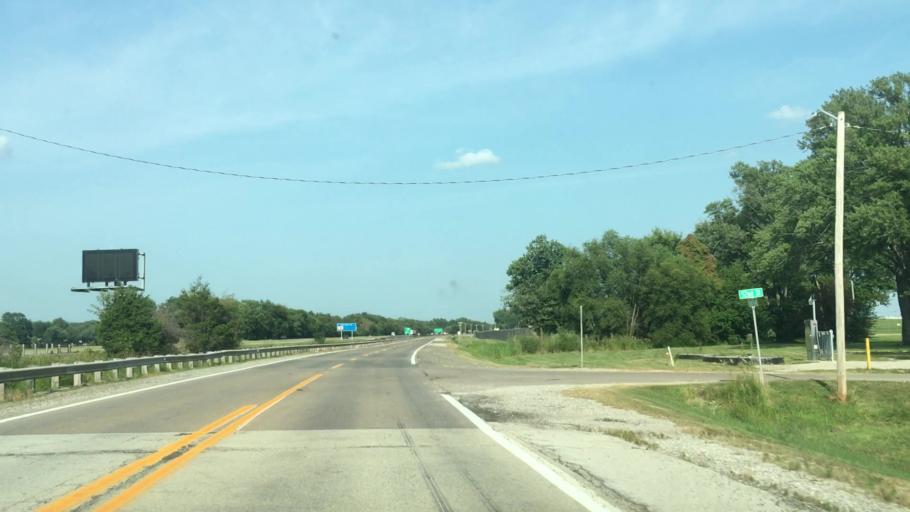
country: US
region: Illinois
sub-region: Rock Island County
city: Milan
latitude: 41.4561
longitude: -90.5215
